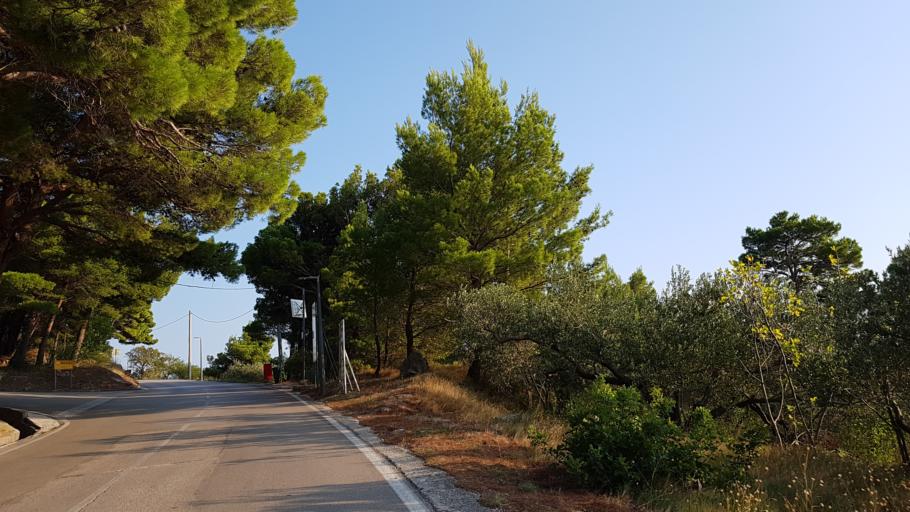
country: HR
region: Splitsko-Dalmatinska
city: Donja Brela
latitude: 43.3808
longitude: 16.9188
